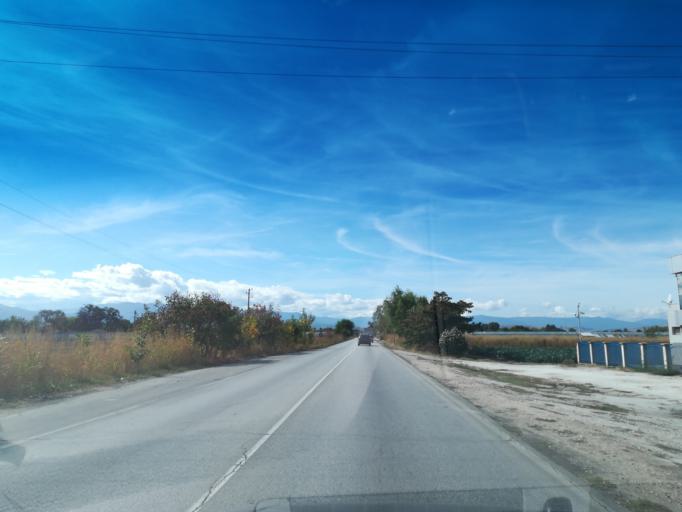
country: BG
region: Plovdiv
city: Stamboliyski
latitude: 42.1217
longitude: 24.5779
